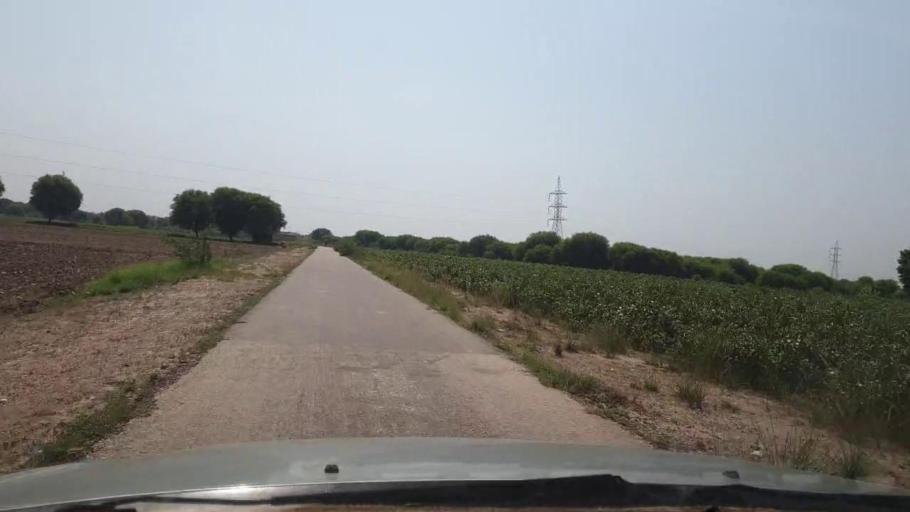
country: PK
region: Sindh
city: Chambar
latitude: 25.2250
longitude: 68.7778
